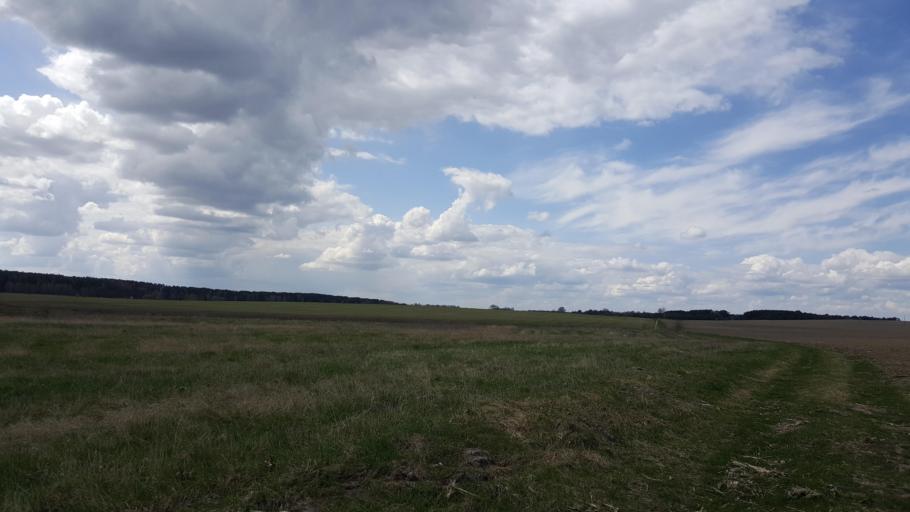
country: BY
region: Brest
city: Kamyanyets
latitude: 52.3511
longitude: 23.7298
